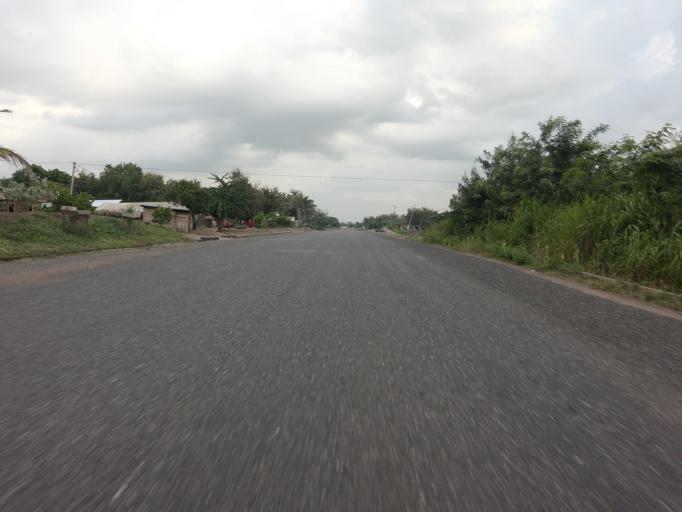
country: GH
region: Volta
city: Ho
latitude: 6.4927
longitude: 0.4874
